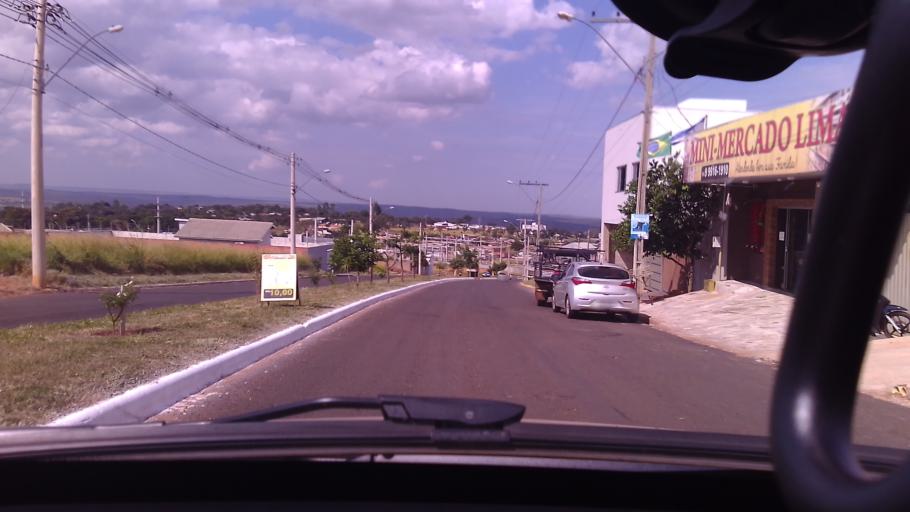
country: BR
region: Goias
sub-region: Mineiros
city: Mineiros
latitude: -17.5470
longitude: -52.5325
